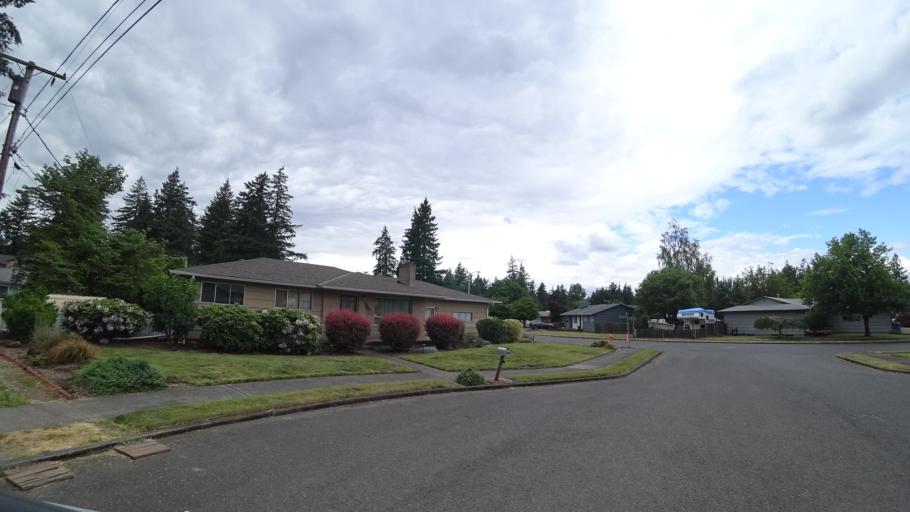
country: US
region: Oregon
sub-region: Clackamas County
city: Happy Valley
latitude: 45.4963
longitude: -122.5001
